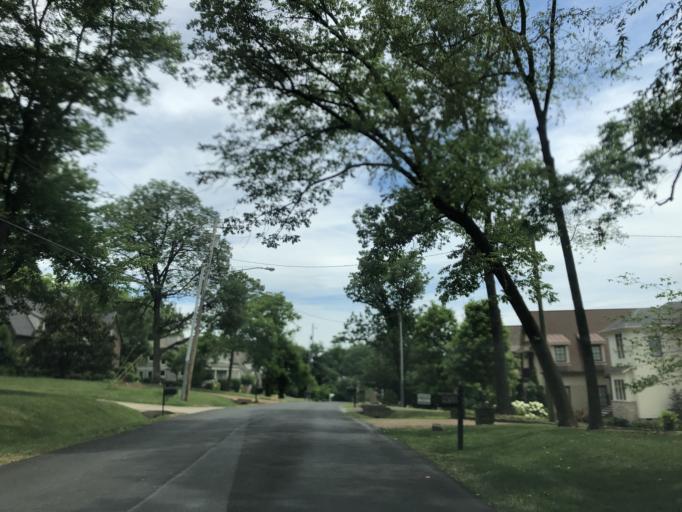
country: US
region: Tennessee
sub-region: Davidson County
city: Oak Hill
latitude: 36.1087
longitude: -86.8066
